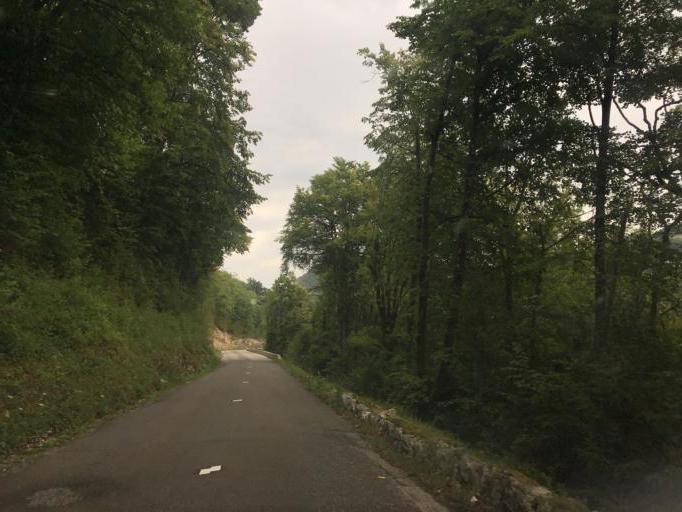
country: FR
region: Franche-Comte
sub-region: Departement du Jura
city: Lavans-les-Saint-Claude
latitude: 46.3341
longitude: 5.7638
